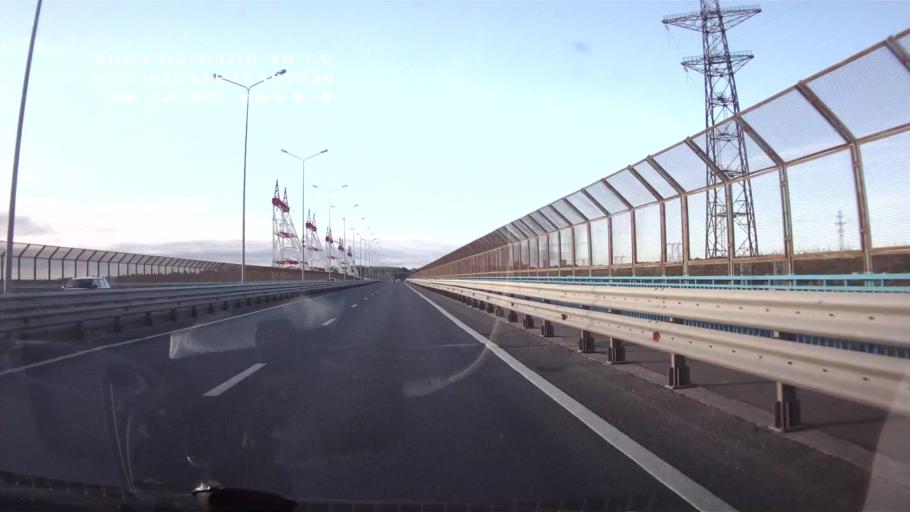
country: RU
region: Chuvashia
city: Novocheboksarsk
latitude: 56.1428
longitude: 47.4655
